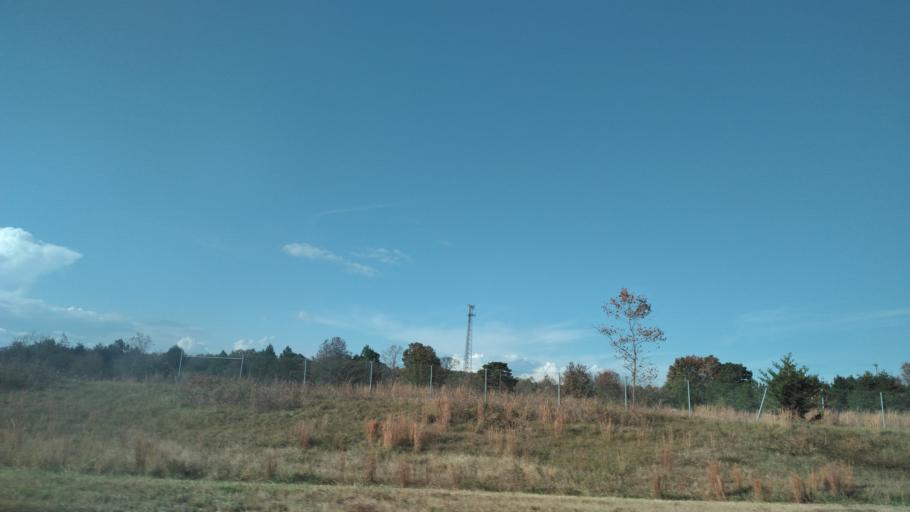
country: US
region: South Carolina
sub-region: Spartanburg County
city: Fairforest
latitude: 34.9616
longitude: -82.0516
